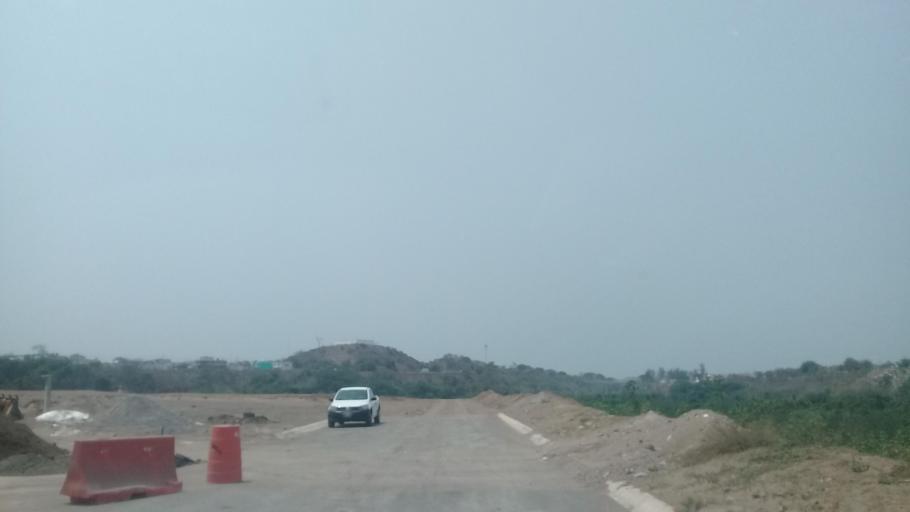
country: MX
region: Veracruz
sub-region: Veracruz
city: Lomas de Rio Medio Cuatro
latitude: 19.1927
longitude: -96.2060
